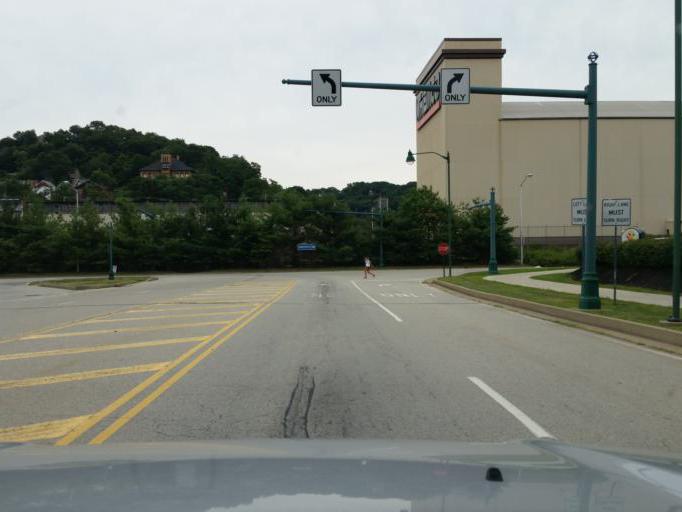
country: US
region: Pennsylvania
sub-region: Allegheny County
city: Homestead
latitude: 40.4038
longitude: -79.9200
